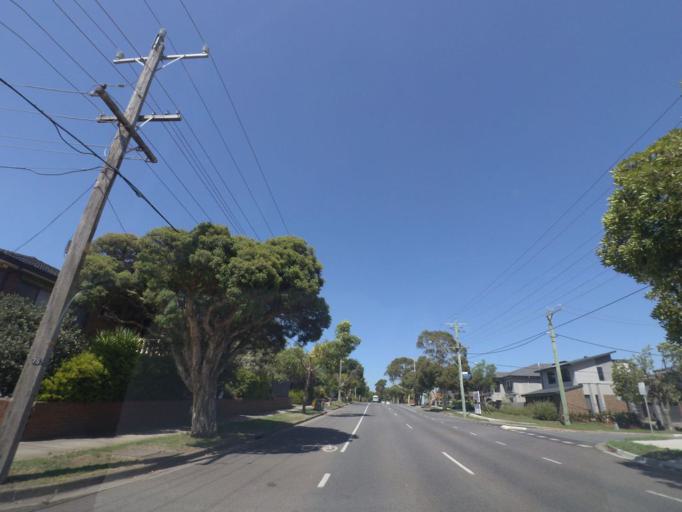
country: AU
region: Victoria
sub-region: Whitehorse
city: Vermont South
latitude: -37.8630
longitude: 145.1773
